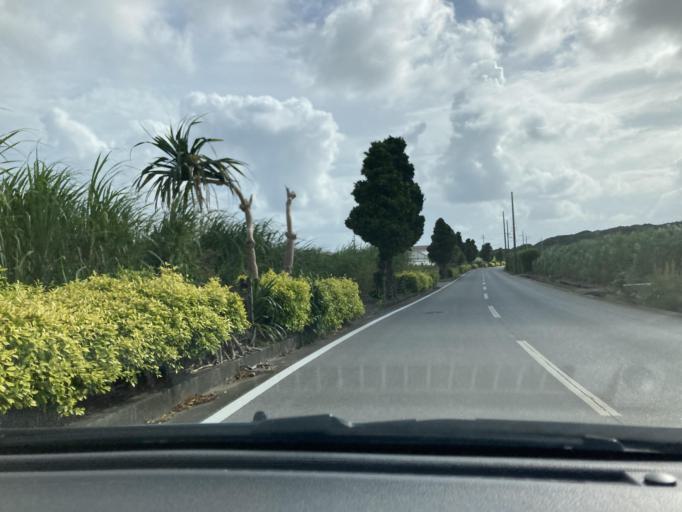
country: JP
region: Okinawa
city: Itoman
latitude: 26.0894
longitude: 127.6941
